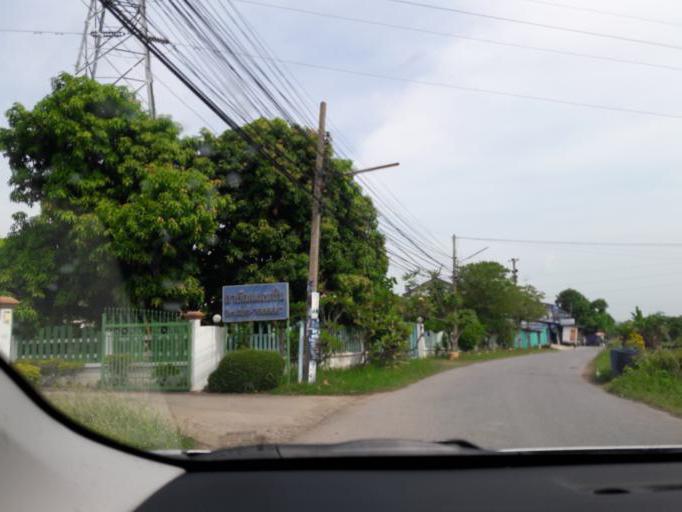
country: TH
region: Ang Thong
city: Ang Thong
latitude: 14.5797
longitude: 100.4743
